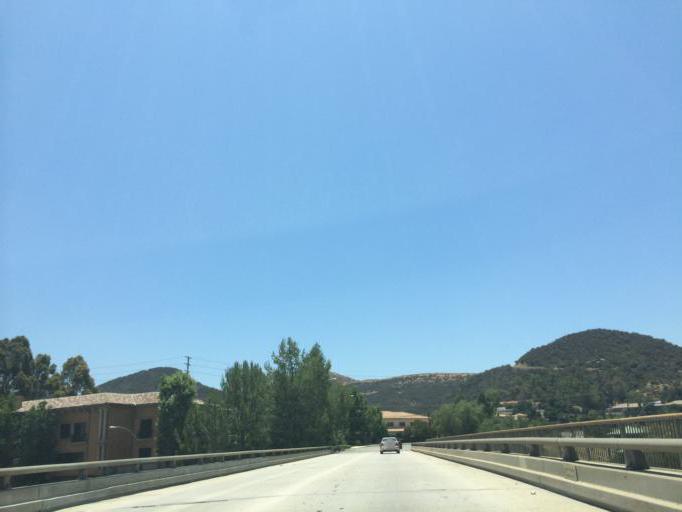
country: US
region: California
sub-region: Los Angeles County
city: Agoura
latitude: 34.1435
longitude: -118.7380
